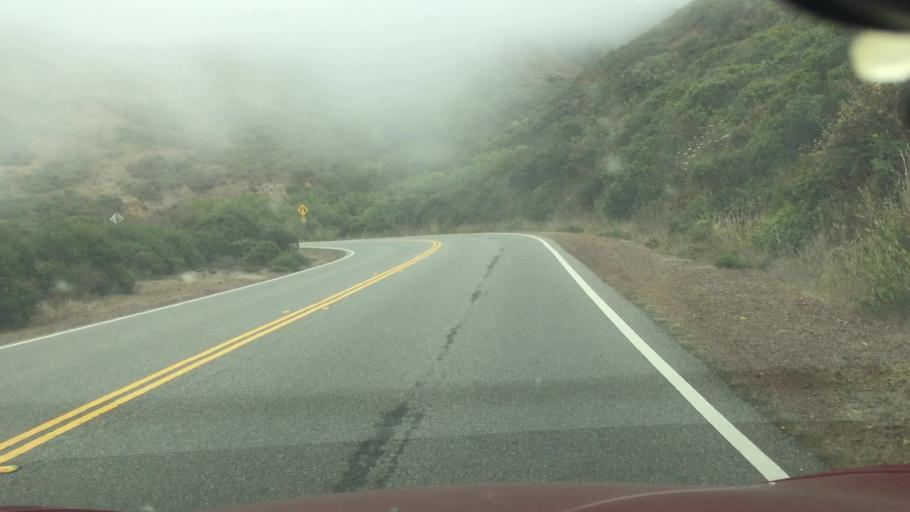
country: US
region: California
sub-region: Marin County
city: Sausalito
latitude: 37.8371
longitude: -122.4969
